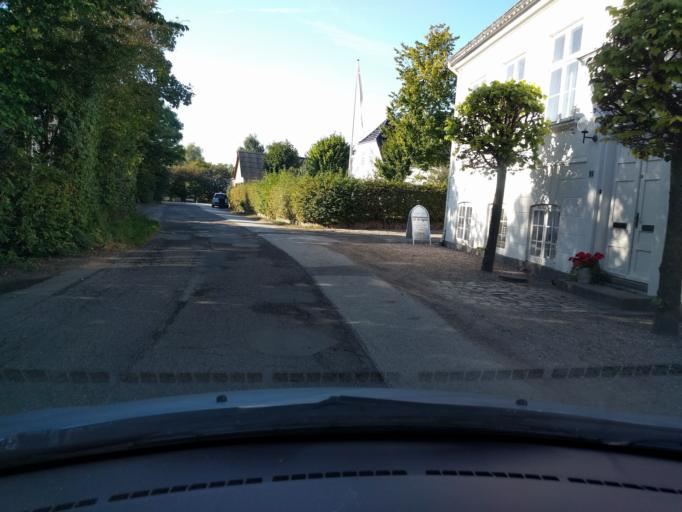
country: DK
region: South Denmark
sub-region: Assens Kommune
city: Harby
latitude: 55.1410
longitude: 10.0212
